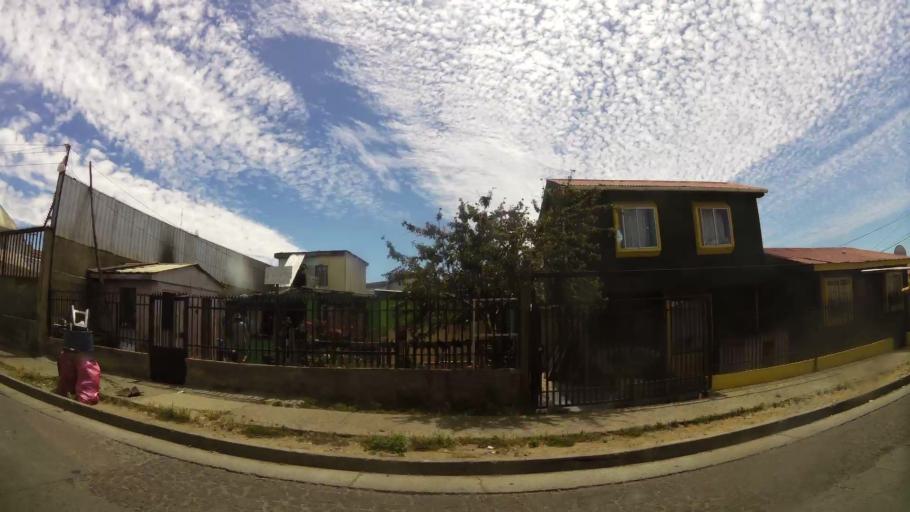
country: CL
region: Valparaiso
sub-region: Provincia de Valparaiso
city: Vina del Mar
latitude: -33.0646
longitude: -71.5697
